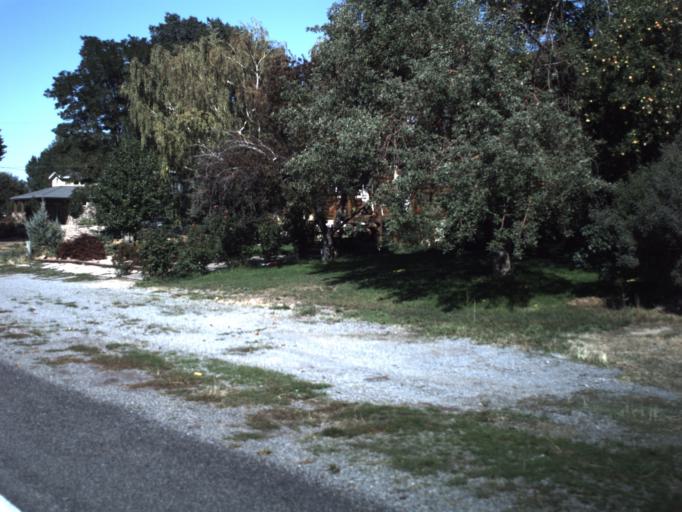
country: US
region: Utah
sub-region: Millard County
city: Fillmore
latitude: 39.0956
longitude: -112.2709
